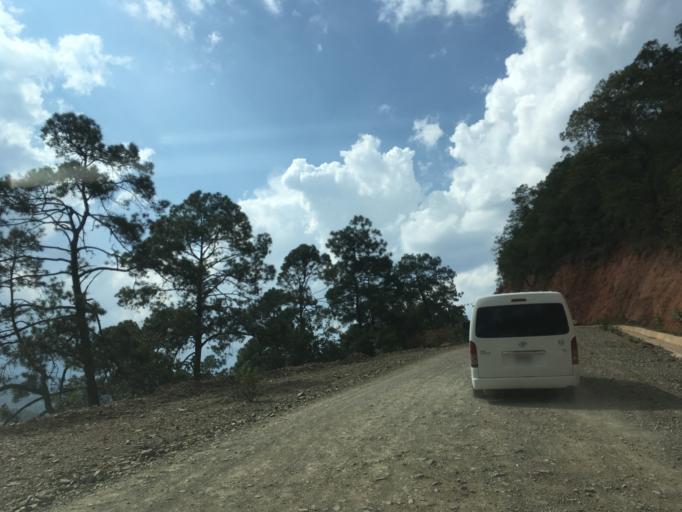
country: MX
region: Oaxaca
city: Santiago Tilantongo
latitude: 17.2009
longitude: -97.2800
